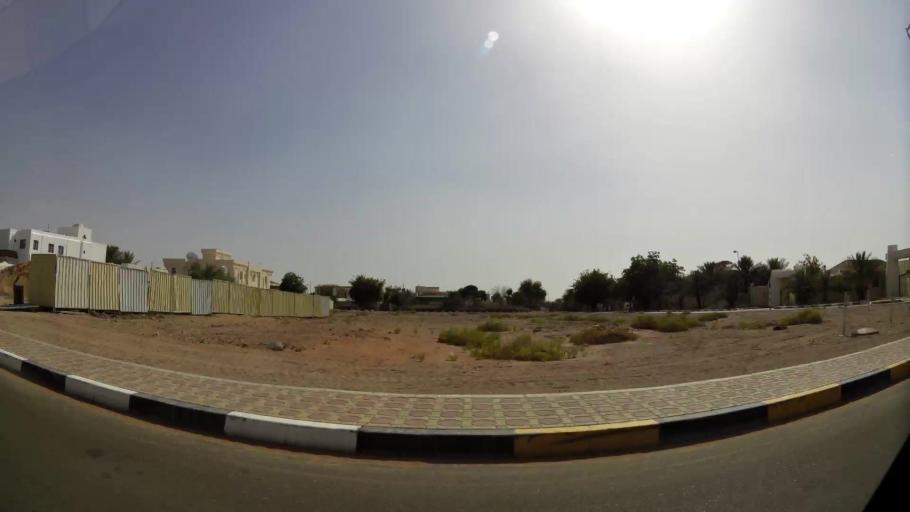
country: AE
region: Abu Dhabi
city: Al Ain
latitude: 24.2424
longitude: 55.6945
